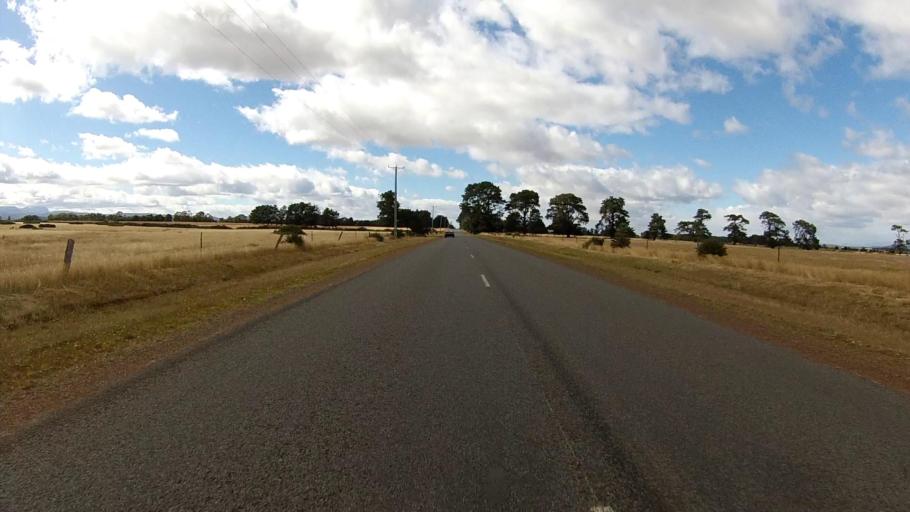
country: AU
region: Tasmania
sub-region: Northern Midlands
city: Evandale
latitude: -41.6012
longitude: 147.2768
